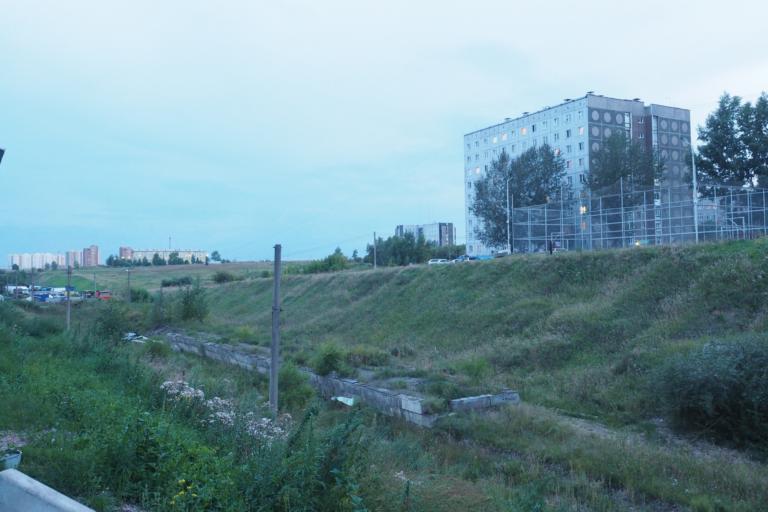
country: RU
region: Krasnoyarskiy
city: Solnechnyy
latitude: 56.1198
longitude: 92.9238
